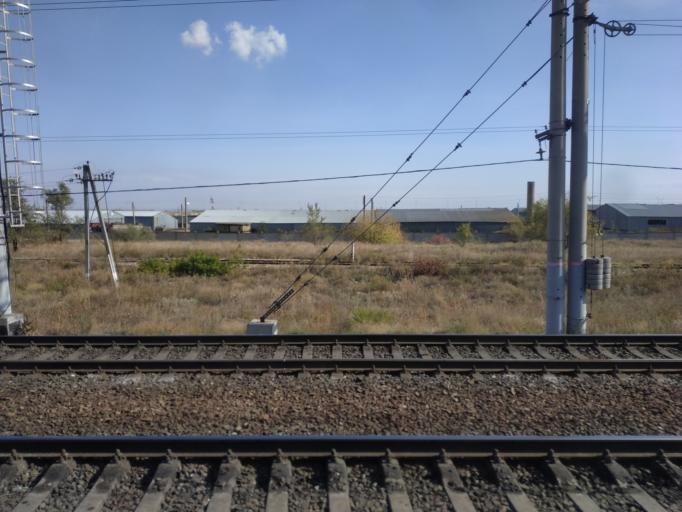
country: RU
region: Volgograd
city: Gumrak
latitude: 48.7889
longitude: 44.3692
